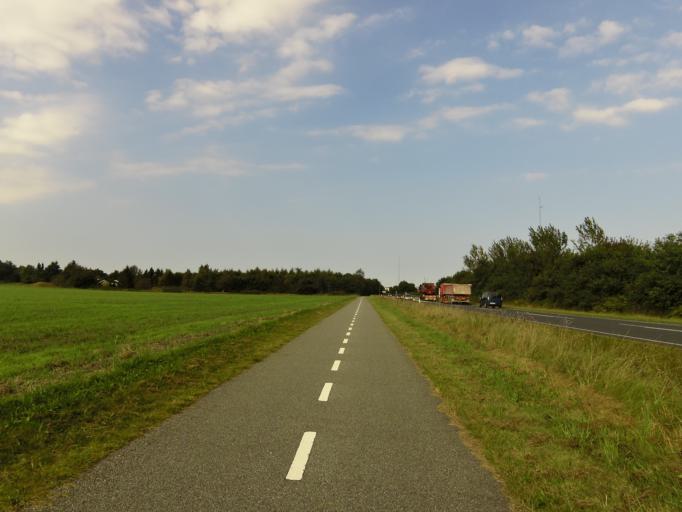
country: DK
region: South Denmark
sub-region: Vejen Kommune
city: Vejen
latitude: 55.4591
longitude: 9.1339
